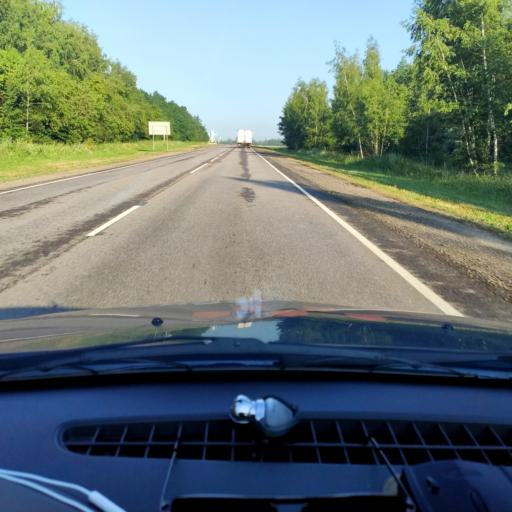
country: RU
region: Lipetsk
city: Izmalkovo
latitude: 52.4373
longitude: 37.8958
